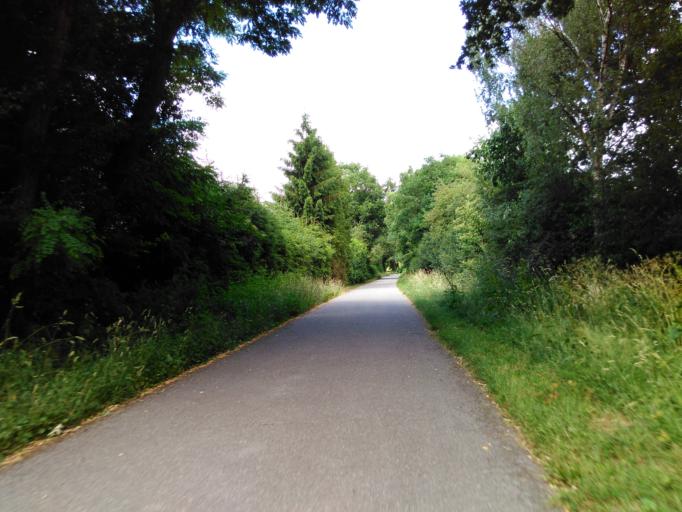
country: LU
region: Luxembourg
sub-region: Canton de Capellen
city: Clemency
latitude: 49.6023
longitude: 5.8772
